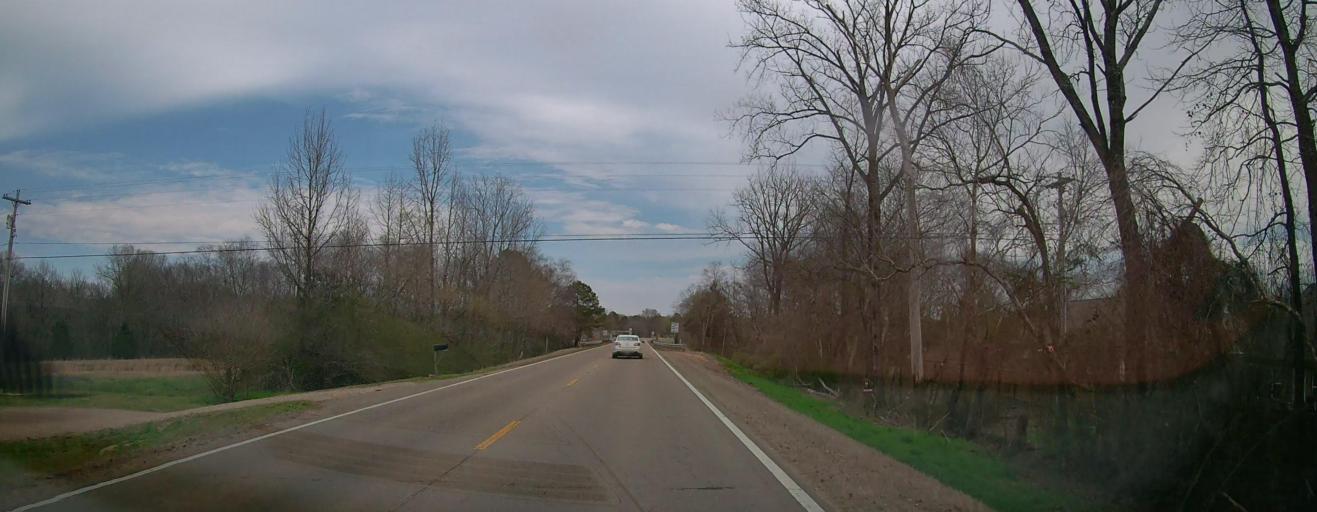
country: US
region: Mississippi
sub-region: Itawamba County
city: Mantachie
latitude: 34.2669
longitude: -88.5642
